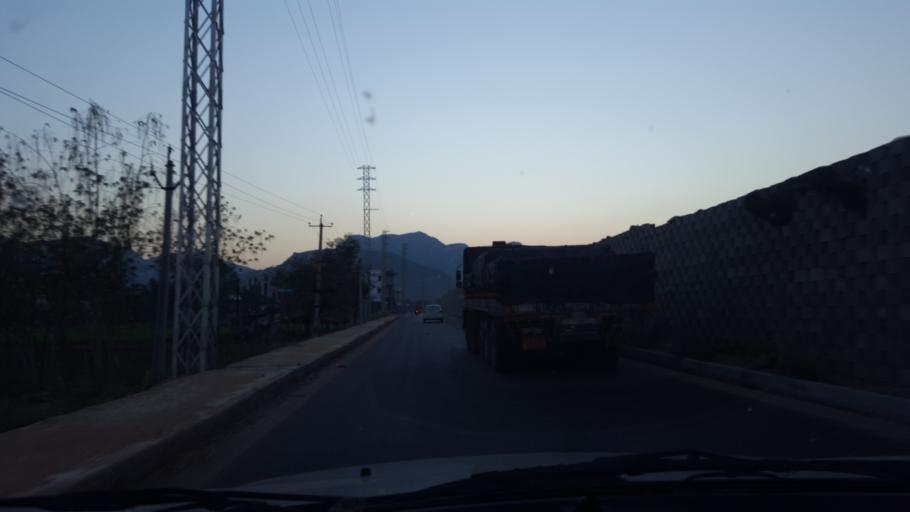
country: IN
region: Andhra Pradesh
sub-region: Chittoor
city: Narasingapuram
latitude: 13.5807
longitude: 79.3178
